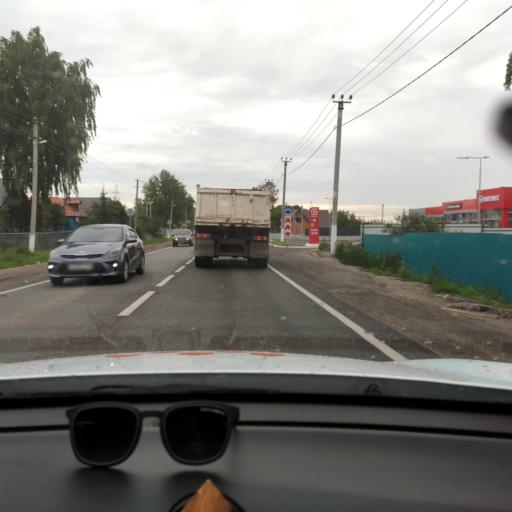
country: RU
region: Tatarstan
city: Vysokaya Gora
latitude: 55.8154
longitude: 49.4578
